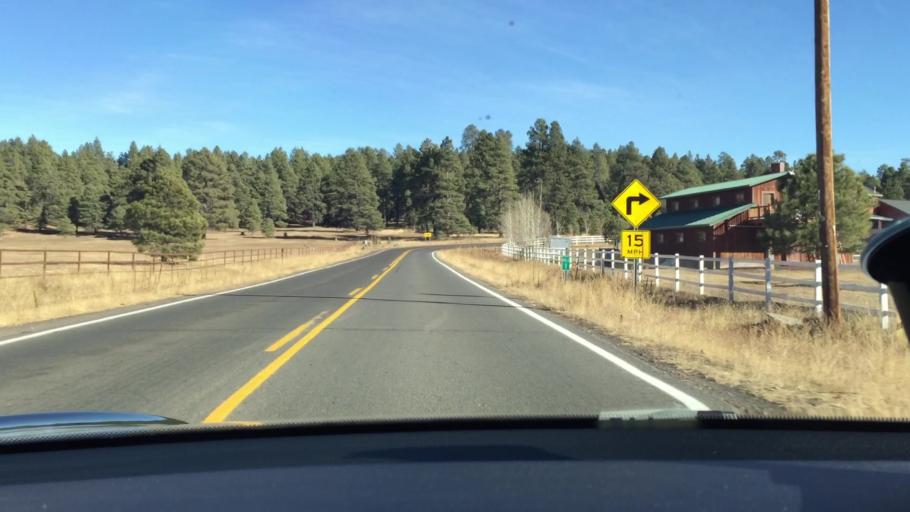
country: US
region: Arizona
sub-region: Coconino County
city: Mountainaire
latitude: 35.0922
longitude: -111.6683
